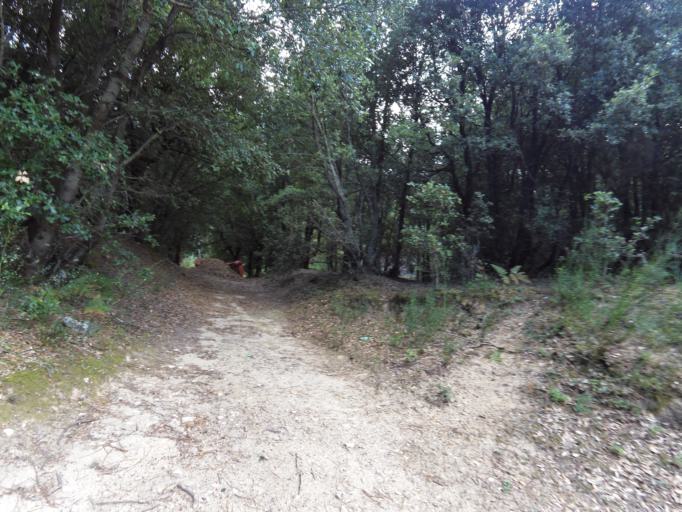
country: IT
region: Calabria
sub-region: Provincia di Reggio Calabria
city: Pazzano
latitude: 38.4790
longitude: 16.4019
